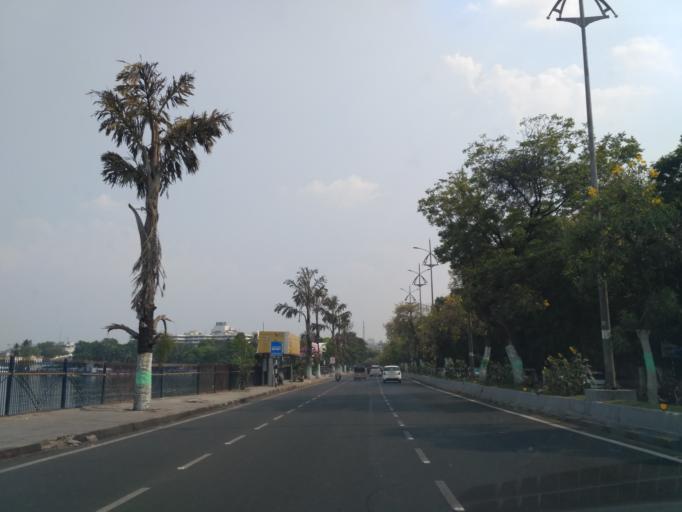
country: IN
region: Telangana
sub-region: Hyderabad
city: Hyderabad
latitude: 17.4133
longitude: 78.4710
